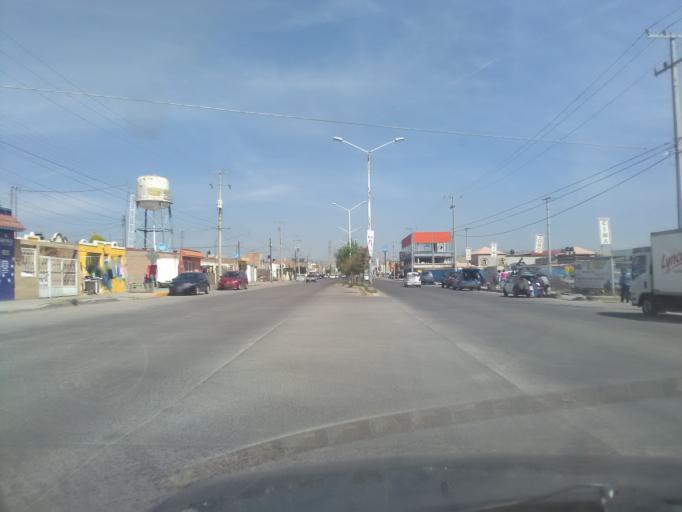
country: MX
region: Durango
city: Victoria de Durango
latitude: 24.0574
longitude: -104.6297
